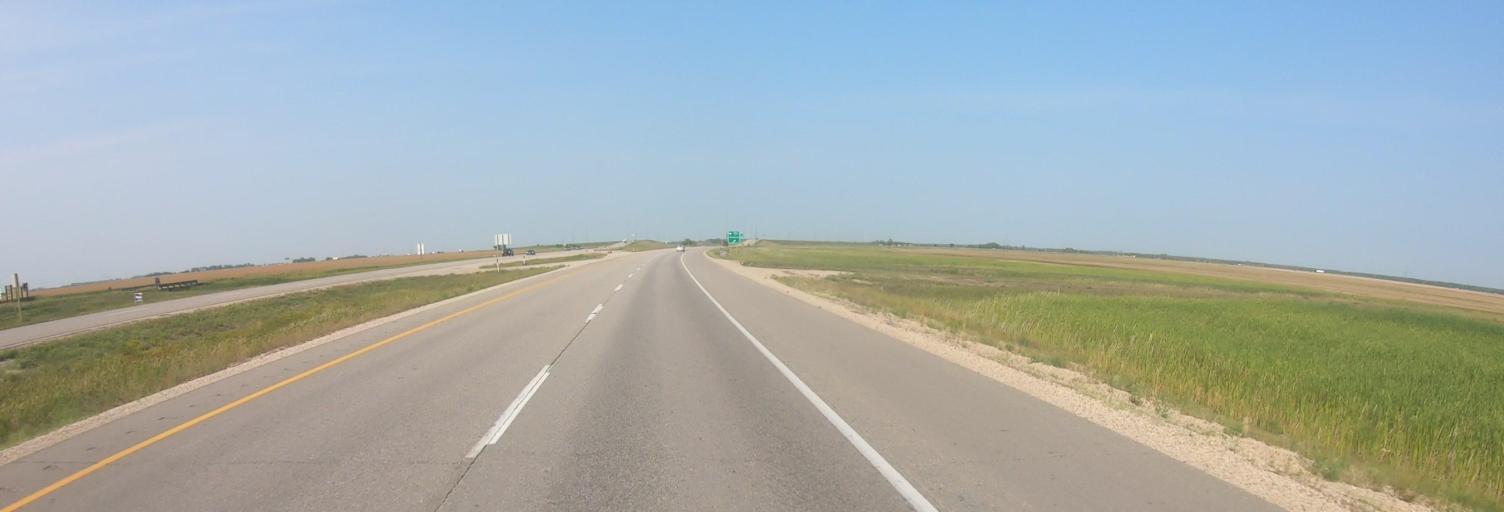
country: CA
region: Manitoba
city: Steinbach
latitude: 49.6922
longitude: -96.6529
